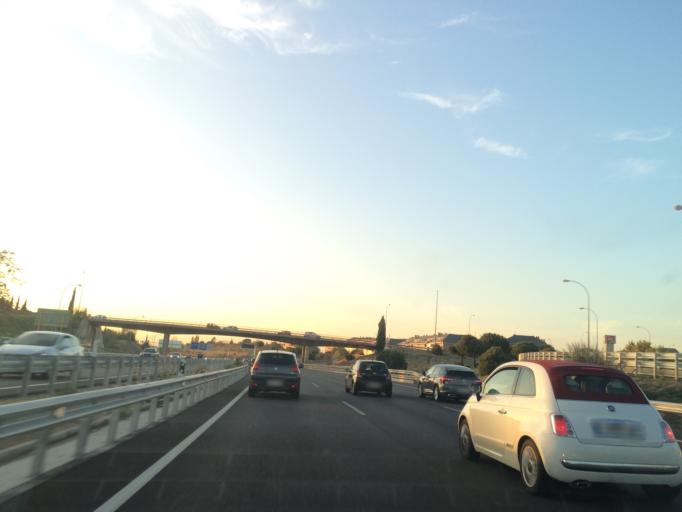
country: ES
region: Madrid
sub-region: Provincia de Madrid
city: Majadahonda
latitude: 40.4487
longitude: -3.8568
